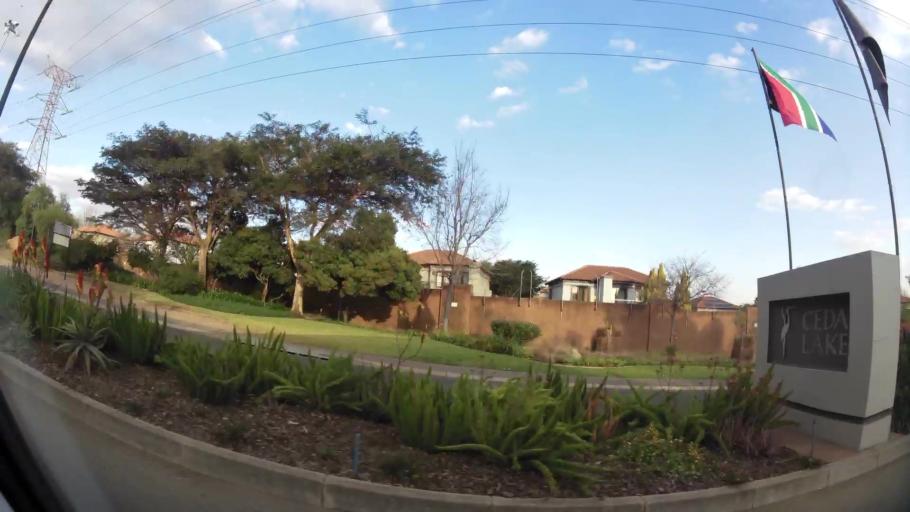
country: ZA
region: Gauteng
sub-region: City of Johannesburg Metropolitan Municipality
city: Diepsloot
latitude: -26.0037
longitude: 27.9860
